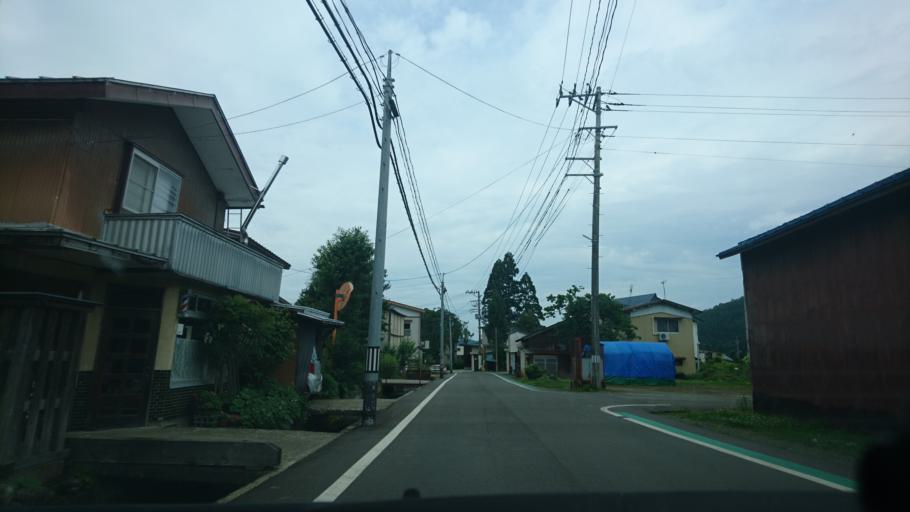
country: JP
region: Akita
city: Yuzawa
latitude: 39.1811
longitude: 140.6450
